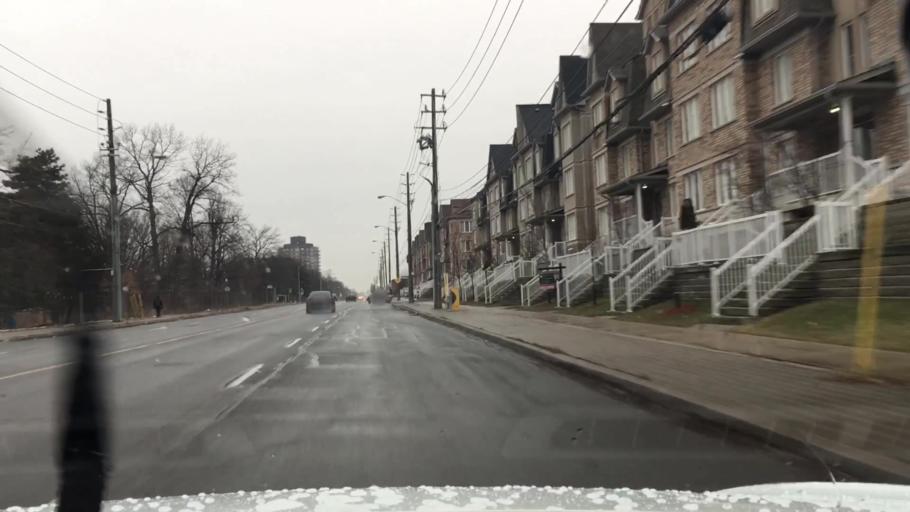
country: CA
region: Ontario
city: Scarborough
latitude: 43.7003
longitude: -79.2761
